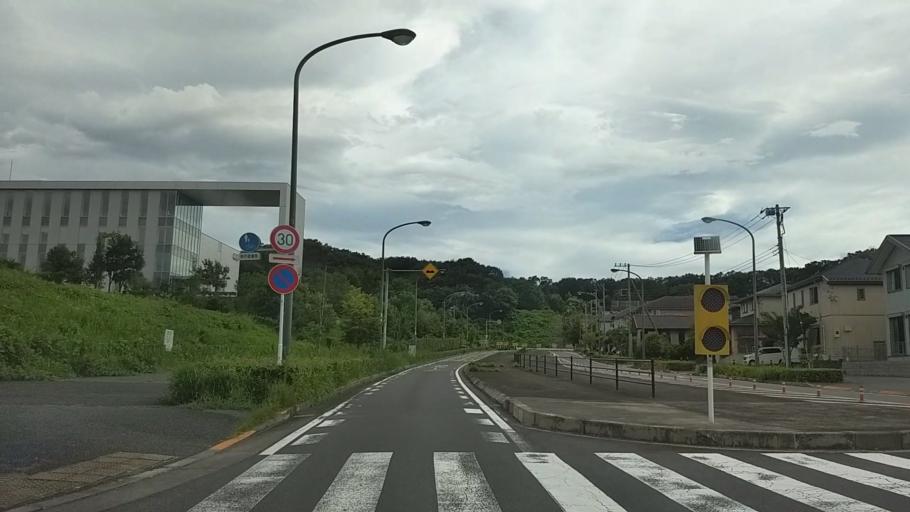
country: JP
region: Tokyo
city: Hachioji
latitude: 35.6190
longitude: 139.3281
